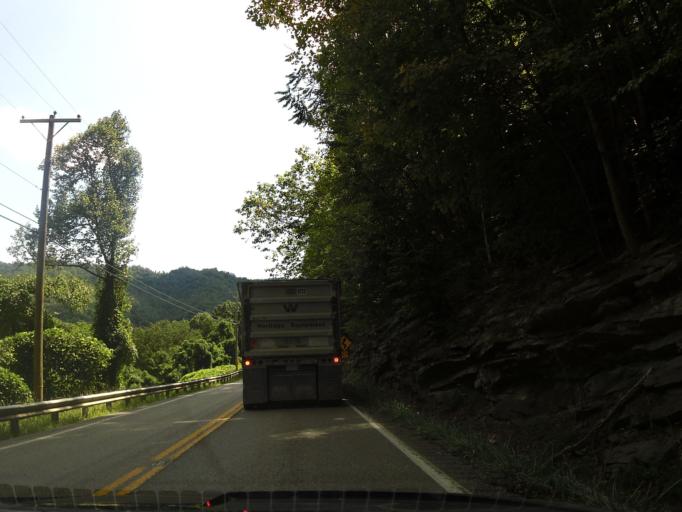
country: US
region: Kentucky
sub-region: Harlan County
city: Harlan
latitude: 36.8747
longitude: -83.3205
